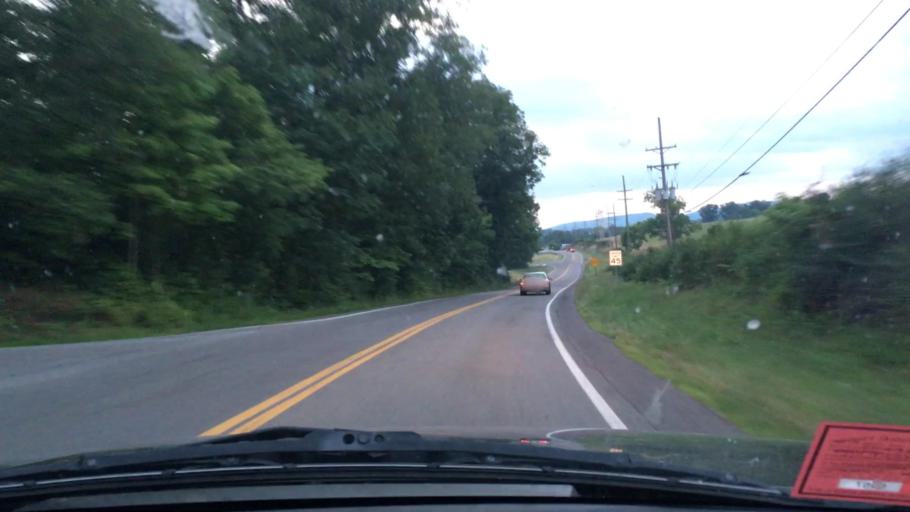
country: US
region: Virginia
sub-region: Pulaski County
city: Dublin
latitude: 37.0647
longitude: -80.7194
